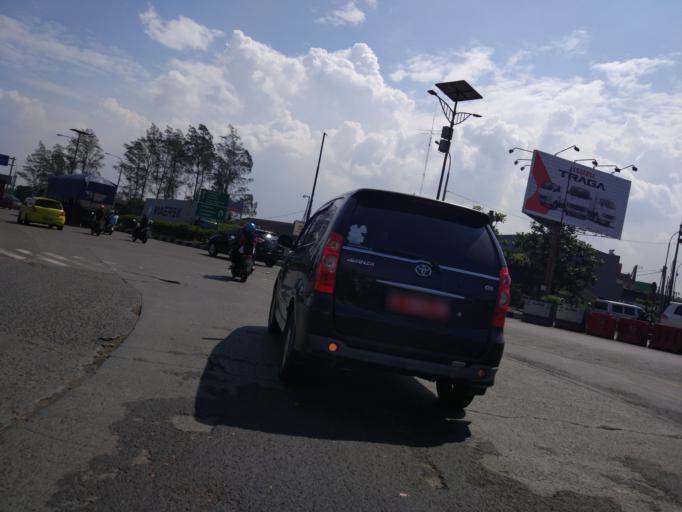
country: ID
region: West Java
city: Cileunyi
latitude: -6.9420
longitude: 107.7551
